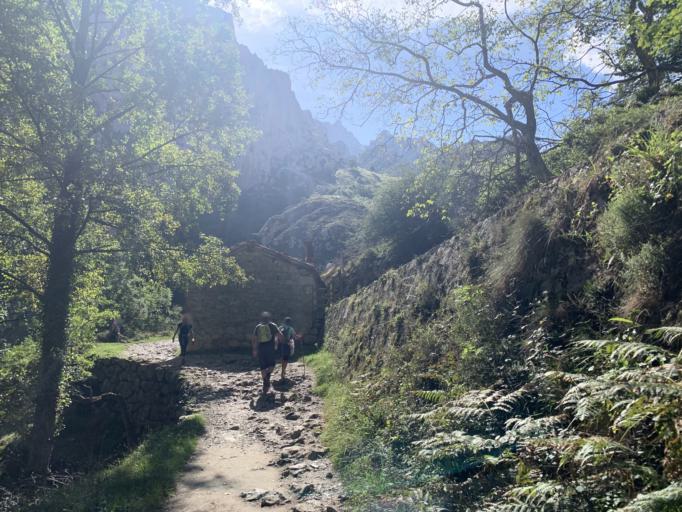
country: ES
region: Asturias
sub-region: Province of Asturias
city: Carrena
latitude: 43.2431
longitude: -4.8897
